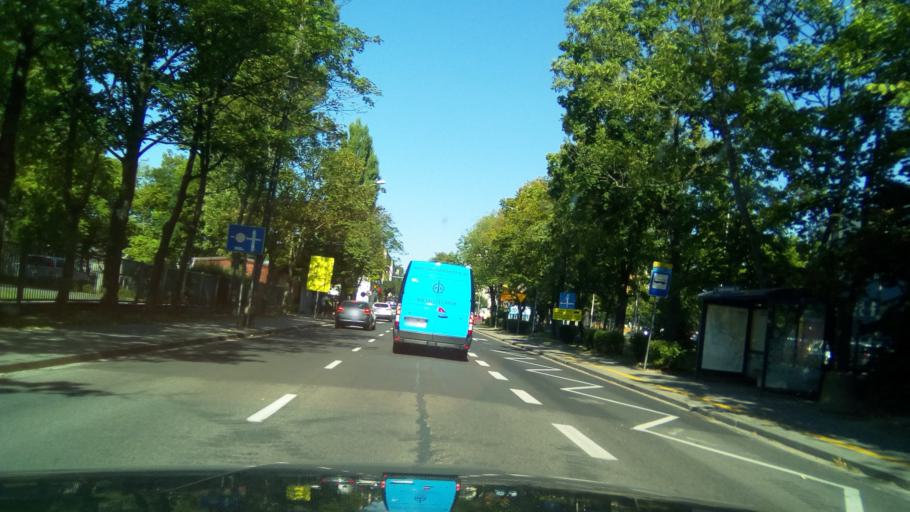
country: PL
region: Masovian Voivodeship
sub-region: Plock
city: Plock
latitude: 52.5404
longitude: 19.7059
